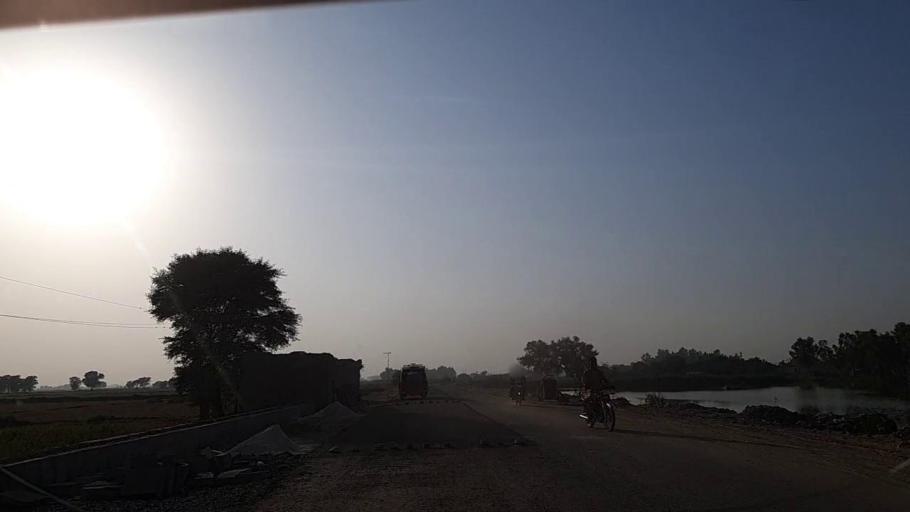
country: PK
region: Sindh
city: Rustam jo Goth
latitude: 27.9635
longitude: 68.8051
